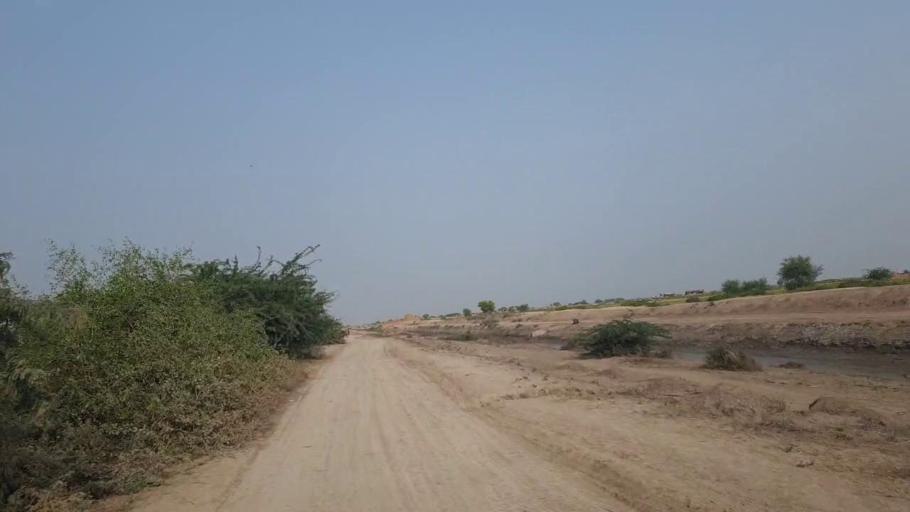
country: PK
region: Sindh
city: Badin
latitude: 24.7076
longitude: 68.7743
